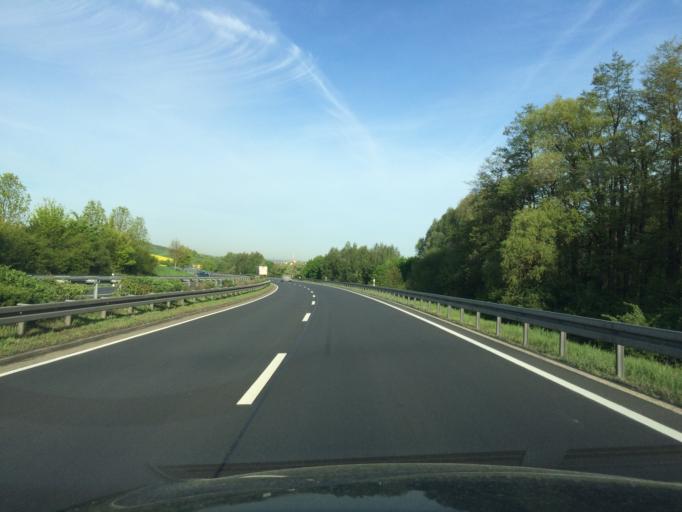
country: DE
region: Bavaria
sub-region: Regierungsbezirk Unterfranken
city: Rottendorf
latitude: 49.7824
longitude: 10.0473
